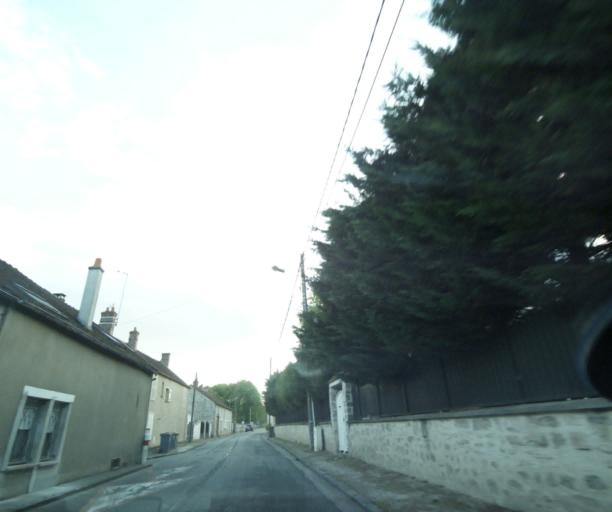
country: FR
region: Ile-de-France
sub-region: Departement de Seine-et-Marne
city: Montigny-sur-Loing
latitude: 48.3403
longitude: 2.7667
